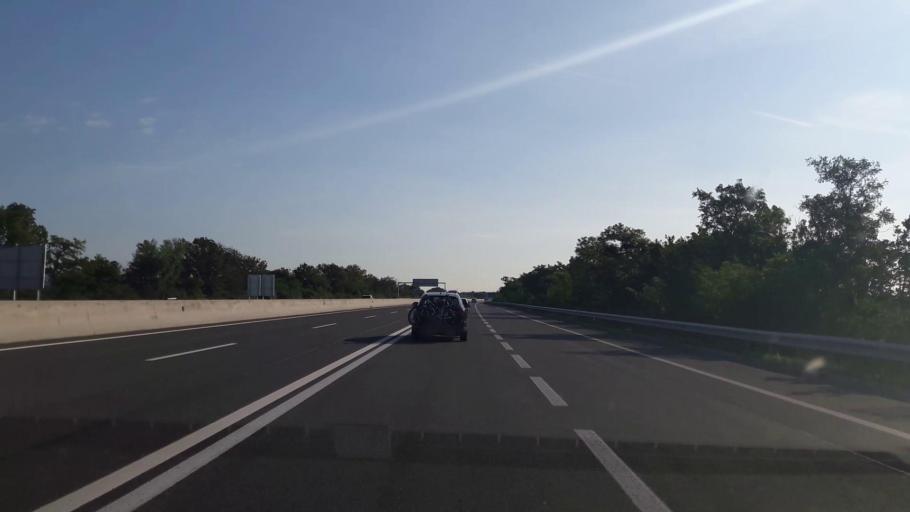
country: AT
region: Burgenland
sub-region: Eisenstadt-Umgebung
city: Wulkaprodersdorf
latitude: 47.8179
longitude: 16.5035
